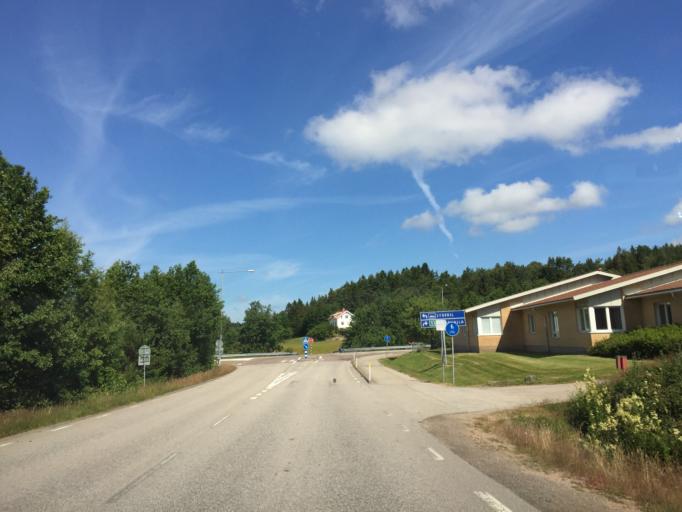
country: SE
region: Vaestra Goetaland
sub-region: Orust
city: Henan
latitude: 58.2923
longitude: 11.5797
